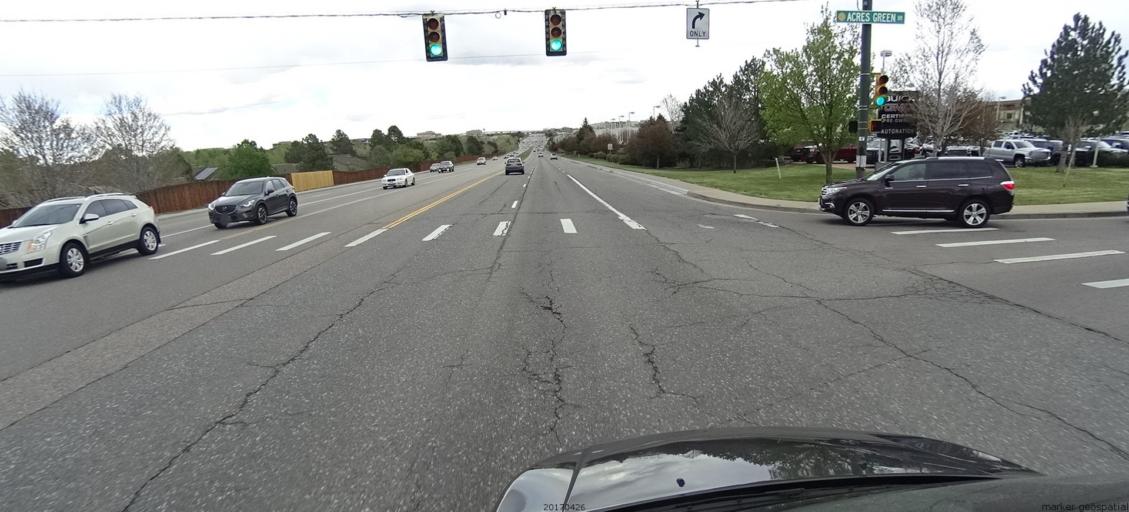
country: US
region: Colorado
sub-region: Douglas County
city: Acres Green
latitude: 39.5659
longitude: -104.8974
